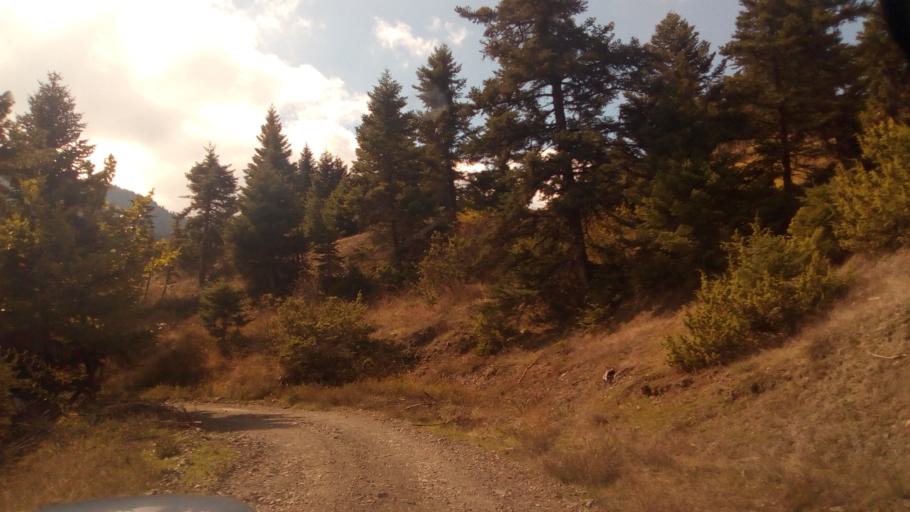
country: GR
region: Central Greece
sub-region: Nomos Fokidos
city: Lidoriki
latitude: 38.6432
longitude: 21.9552
